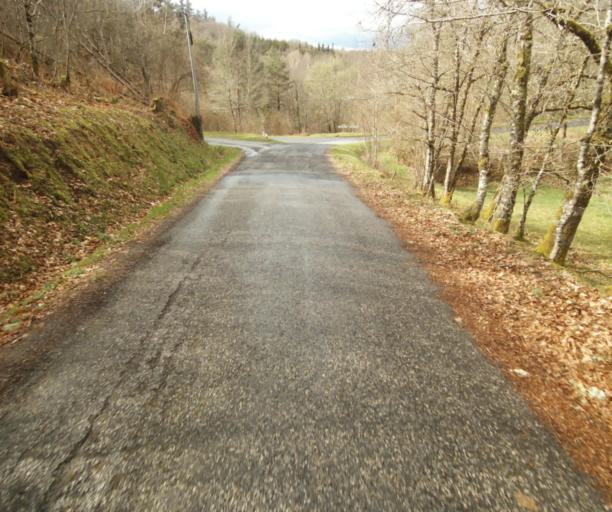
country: FR
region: Limousin
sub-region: Departement de la Correze
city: Saint-Privat
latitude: 45.2545
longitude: 1.9871
